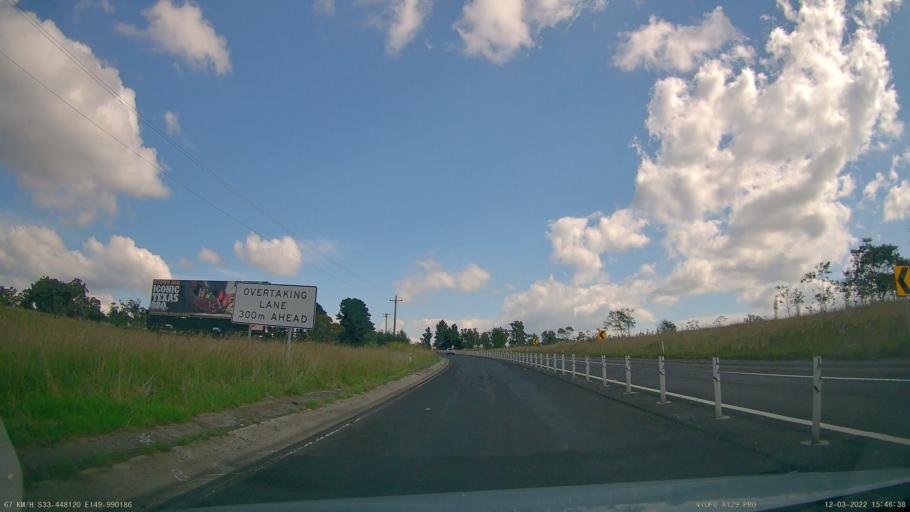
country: AU
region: New South Wales
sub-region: Lithgow
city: Portland
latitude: -33.4484
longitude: 149.9899
